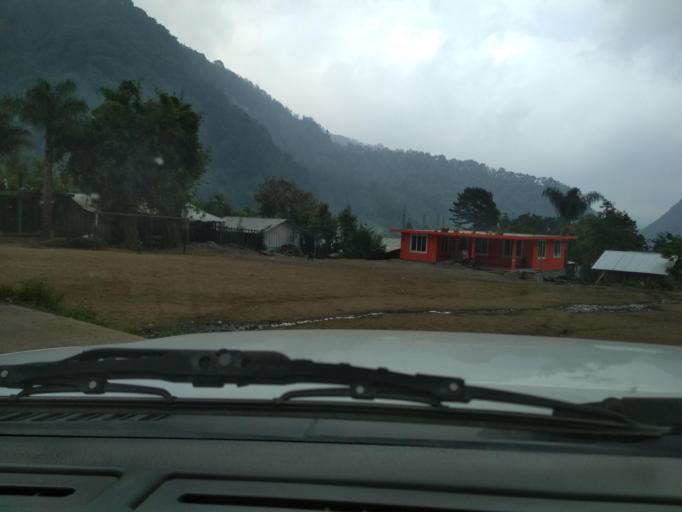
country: MX
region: Veracruz
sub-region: La Perla
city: Metlac Hernandez (Metlac Primero)
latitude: 18.9775
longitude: -97.1432
